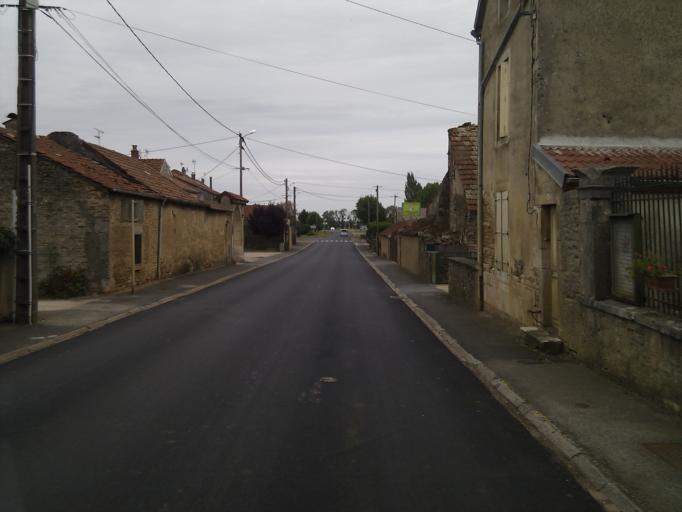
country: FR
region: Lorraine
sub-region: Departement des Vosges
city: Liffol-le-Grand
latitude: 48.2865
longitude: 5.4941
